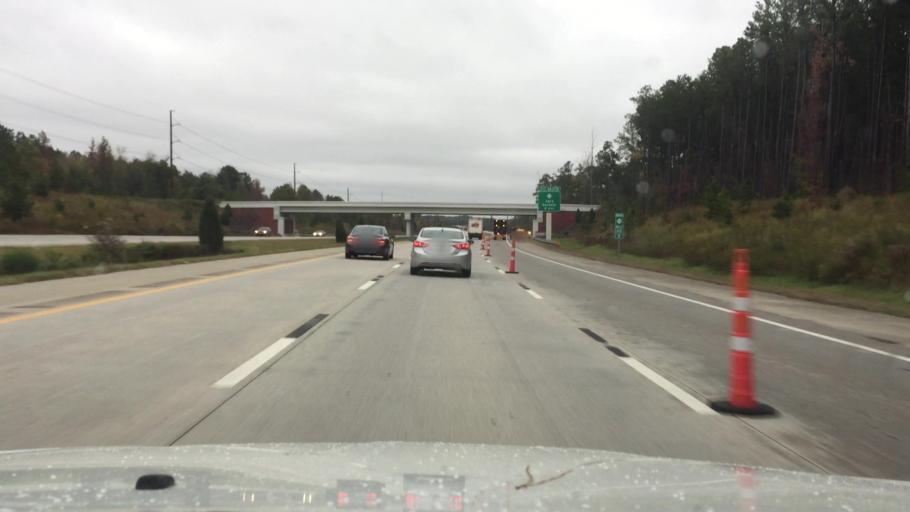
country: US
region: North Carolina
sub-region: Wake County
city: Green Level
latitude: 35.8072
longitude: -78.8920
